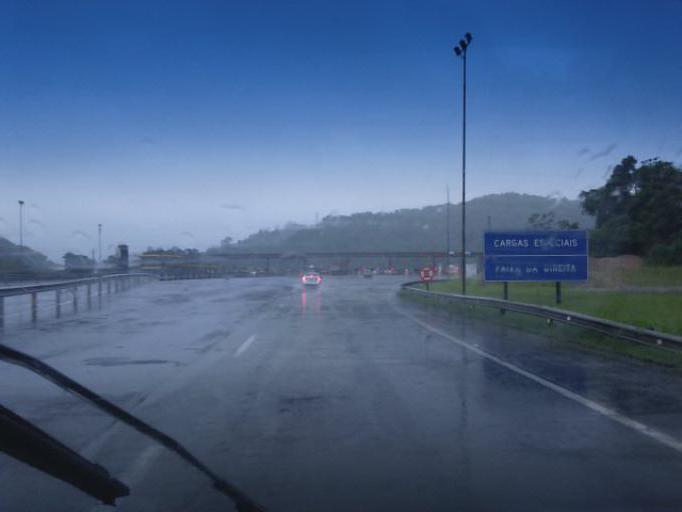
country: BR
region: Sao Paulo
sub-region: Juquia
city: Juquia
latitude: -24.3911
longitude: -47.7231
